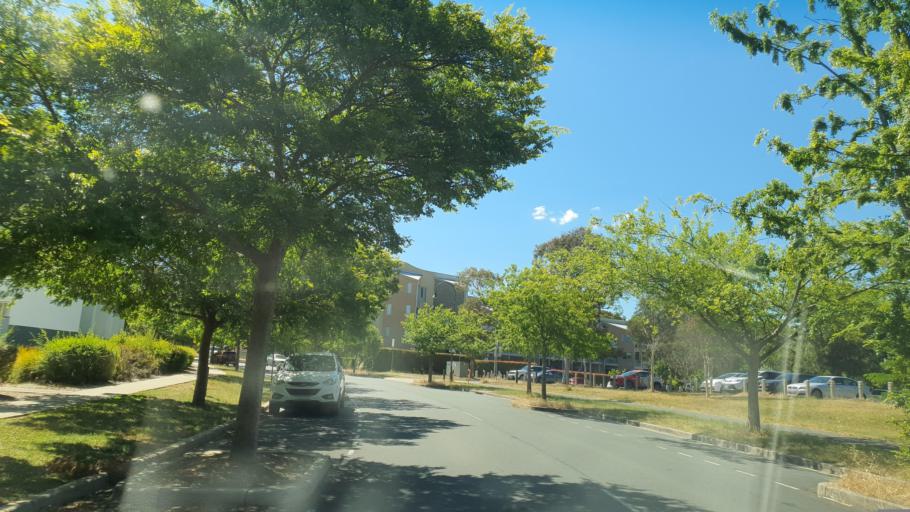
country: AU
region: Australian Capital Territory
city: Macquarie
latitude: -35.2343
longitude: 149.0651
